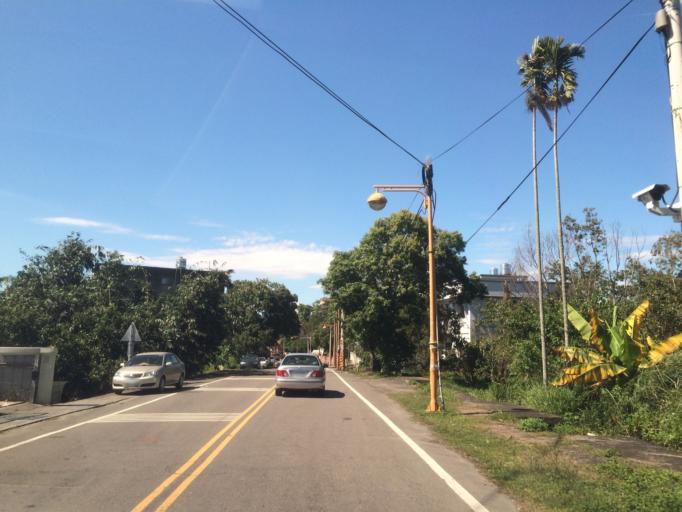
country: TW
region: Taiwan
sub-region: Yunlin
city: Douliu
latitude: 23.7018
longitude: 120.6029
